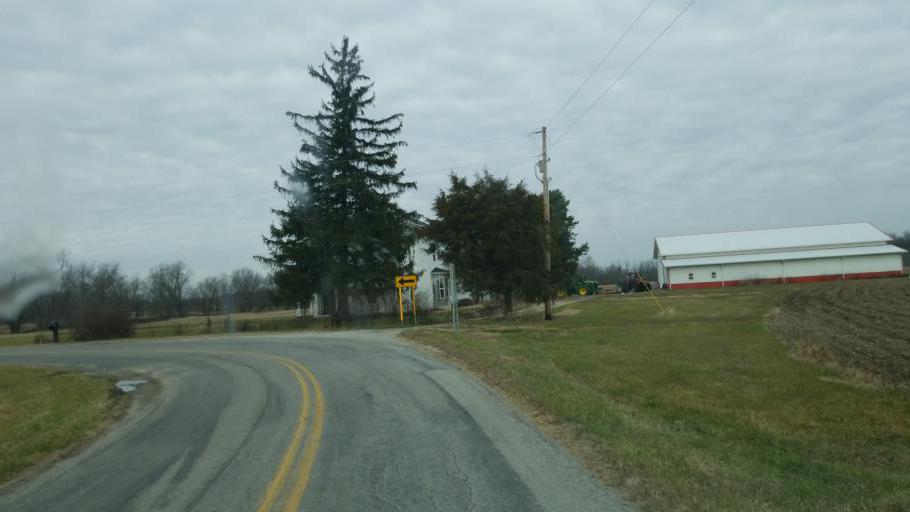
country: US
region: Ohio
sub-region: Union County
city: Richwood
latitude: 40.5622
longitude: -83.3101
